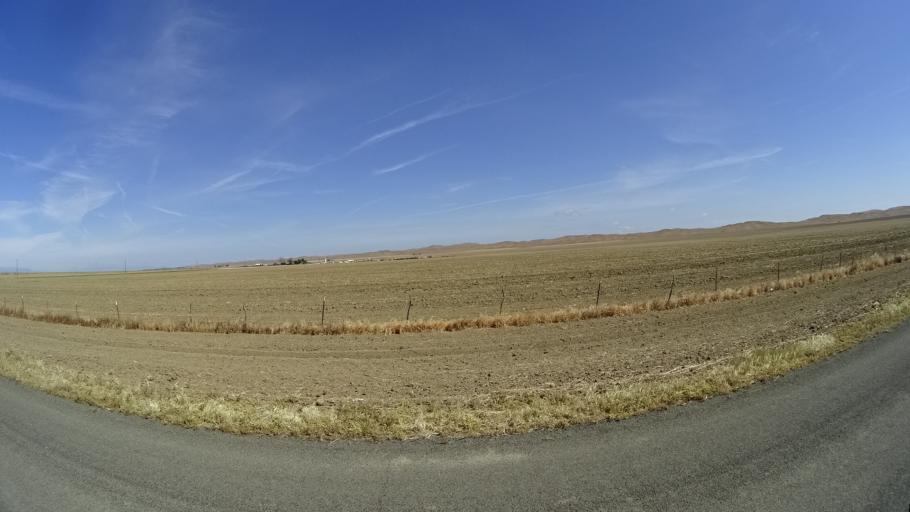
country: US
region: California
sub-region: Kings County
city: Avenal
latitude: 35.9351
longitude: -120.0550
